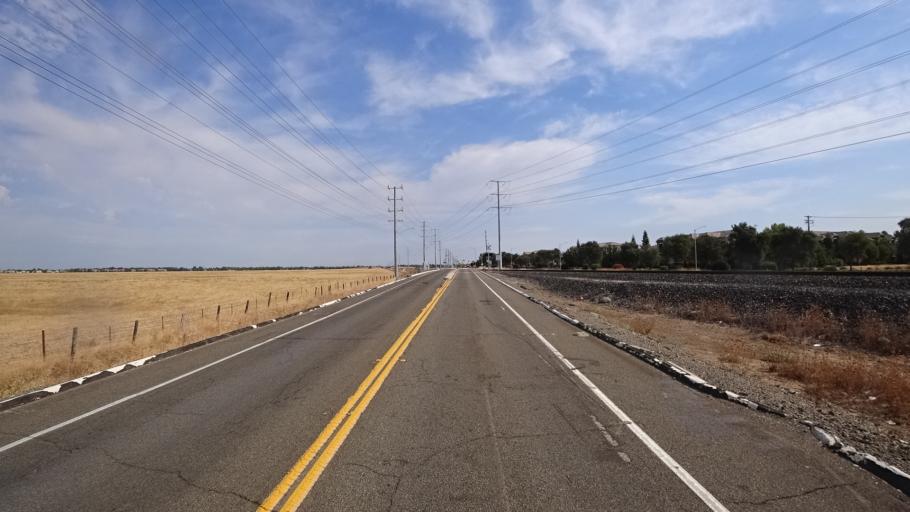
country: US
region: California
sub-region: Sacramento County
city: Laguna
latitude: 38.3908
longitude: -121.4527
